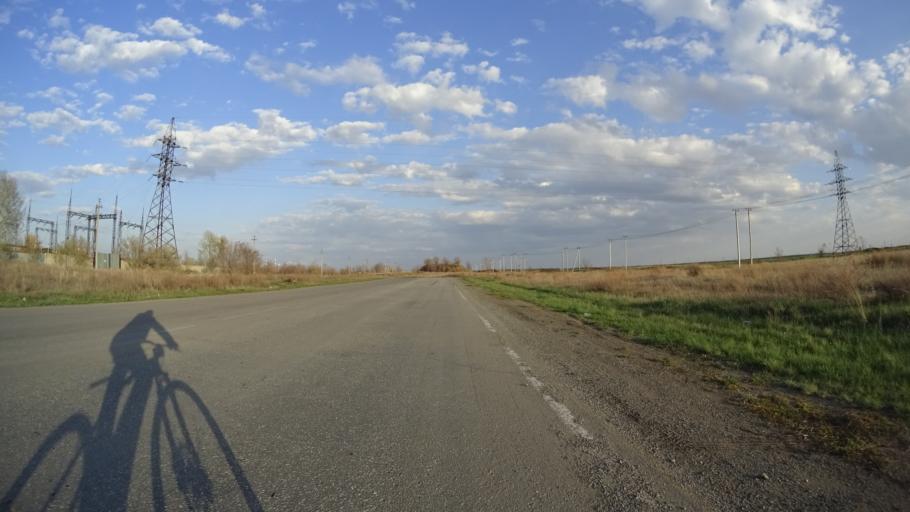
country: RU
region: Chelyabinsk
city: Troitsk
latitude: 54.0628
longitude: 61.5712
